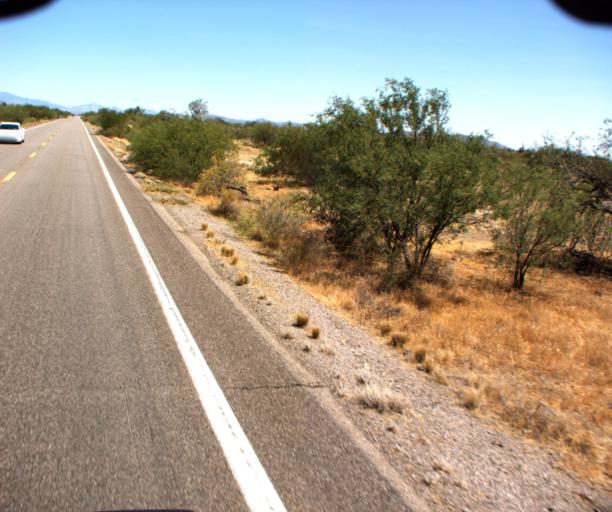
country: US
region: Arizona
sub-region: Pima County
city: Catalina
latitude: 32.7438
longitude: -111.1268
